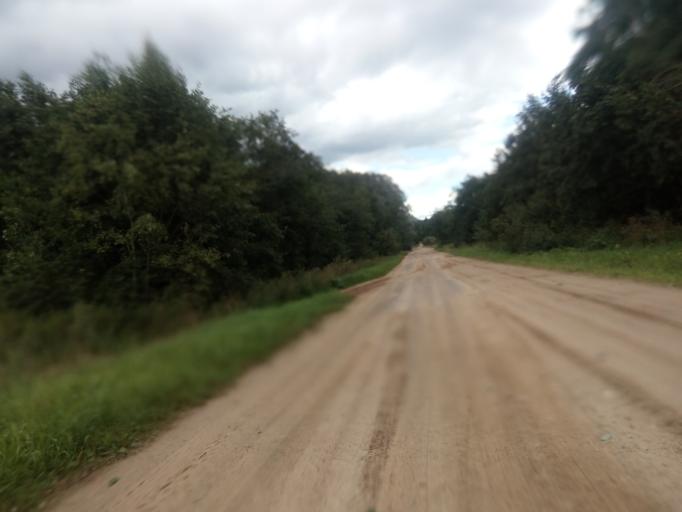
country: BY
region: Vitebsk
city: Dzisna
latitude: 55.7067
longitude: 28.3237
